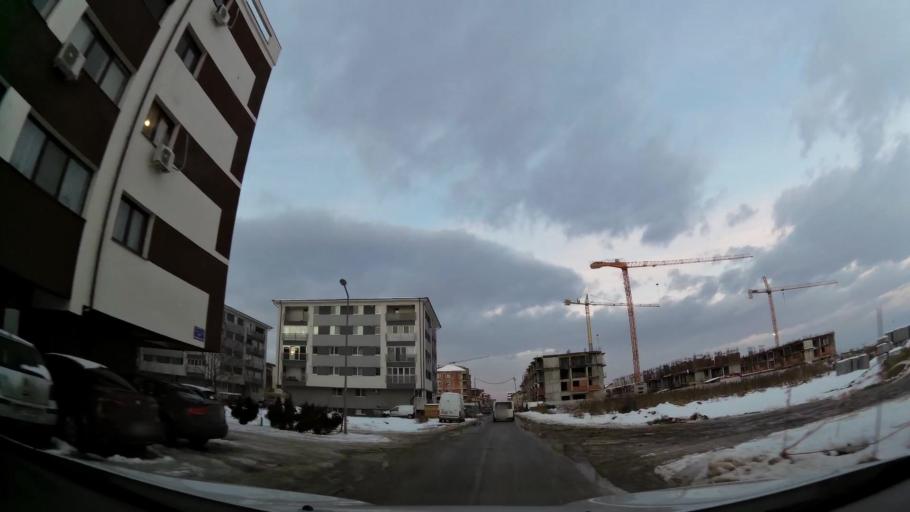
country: RO
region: Ilfov
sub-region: Comuna Popesti-Leordeni
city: Popesti-Leordeni
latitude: 44.3665
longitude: 26.1539
